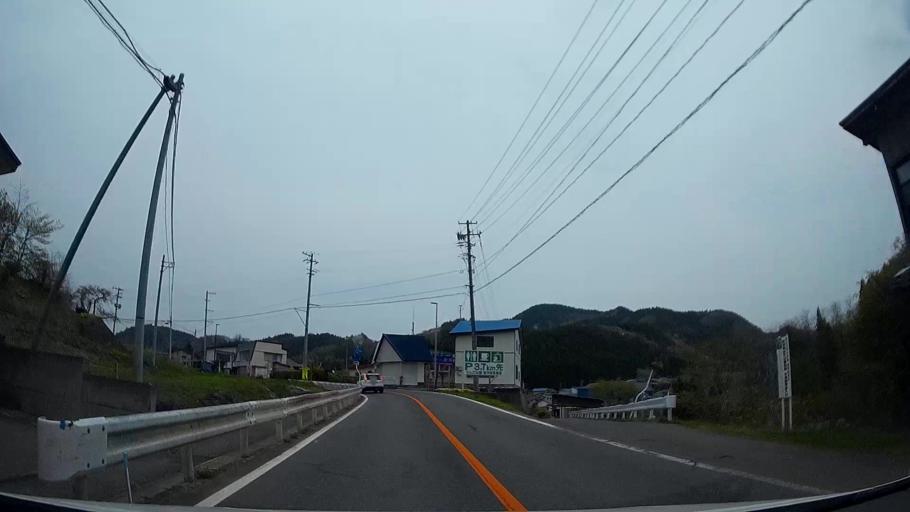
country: JP
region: Akita
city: Hanawa
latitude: 40.3008
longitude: 140.8399
